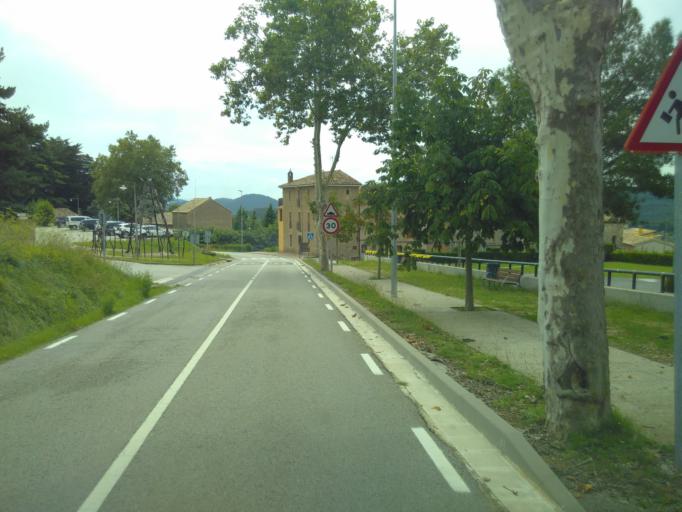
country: ES
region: Catalonia
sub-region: Provincia de Barcelona
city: Alpens
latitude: 42.1208
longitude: 2.1018
